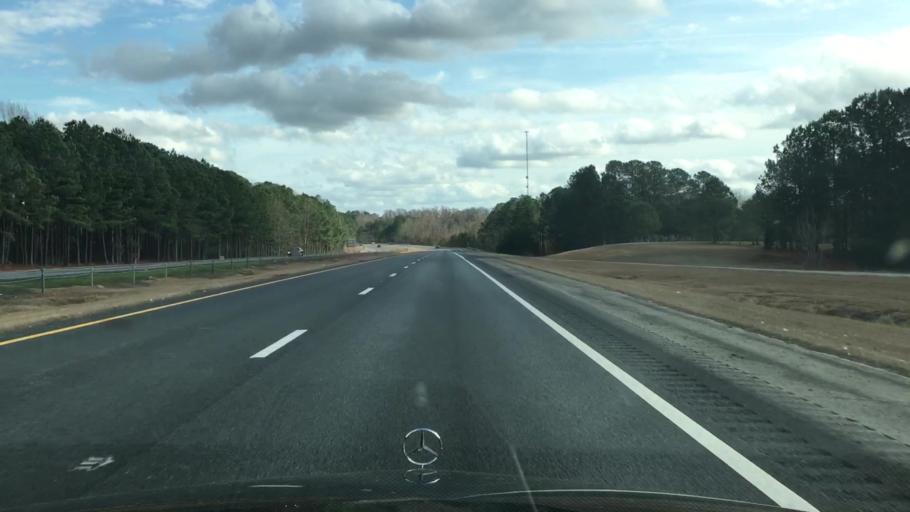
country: US
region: North Carolina
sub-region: Johnston County
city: Benson
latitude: 35.3286
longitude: -78.4465
